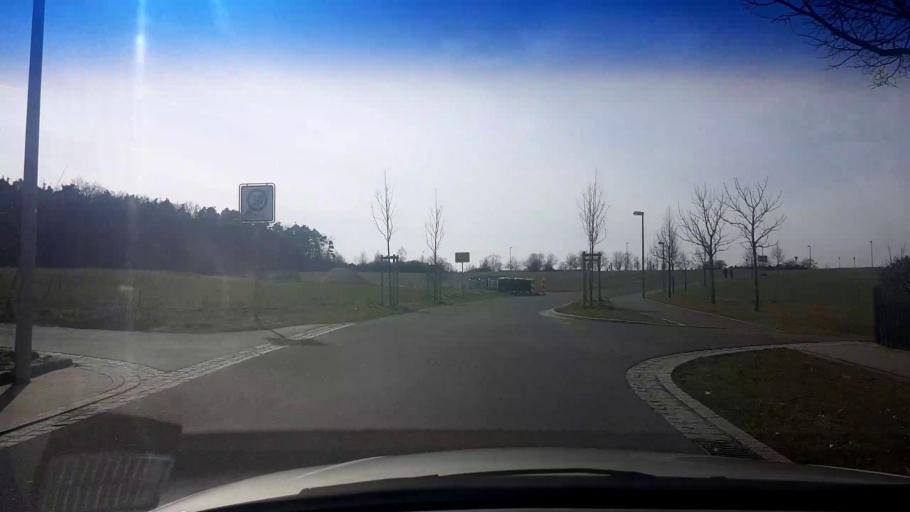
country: DE
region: Bavaria
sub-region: Upper Franconia
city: Burgebrach
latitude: 49.8199
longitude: 10.7379
